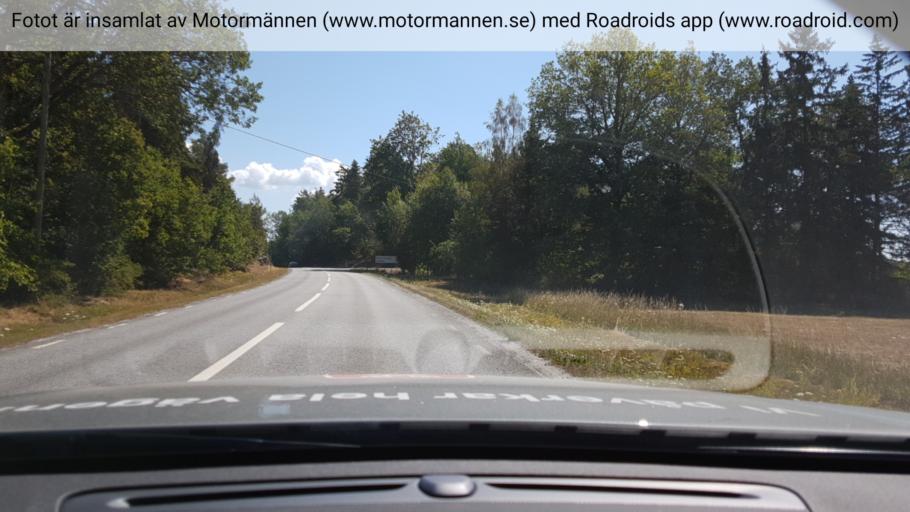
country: SE
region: Stockholm
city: Stenhamra
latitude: 59.3400
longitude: 17.7285
